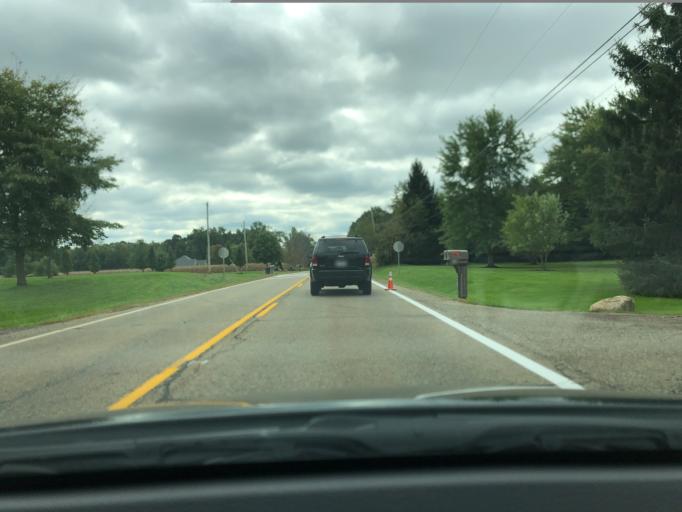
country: US
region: Ohio
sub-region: Stark County
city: Canal Fulton
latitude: 40.8359
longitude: -81.5999
